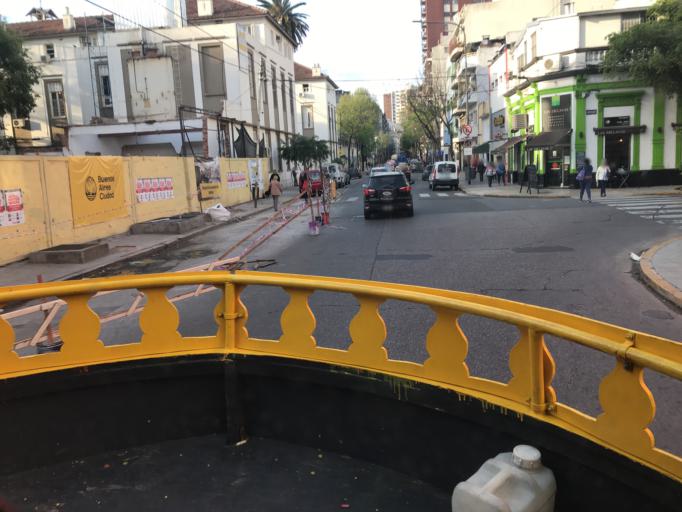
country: AR
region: Buenos Aires F.D.
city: Retiro
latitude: -34.5953
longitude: -58.4106
